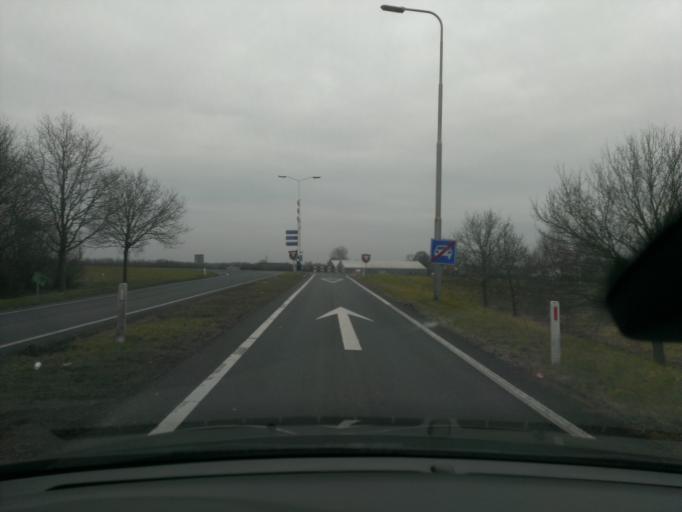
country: NL
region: Overijssel
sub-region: Gemeente Twenterand
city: Vriezenveen
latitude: 52.4041
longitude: 6.6380
